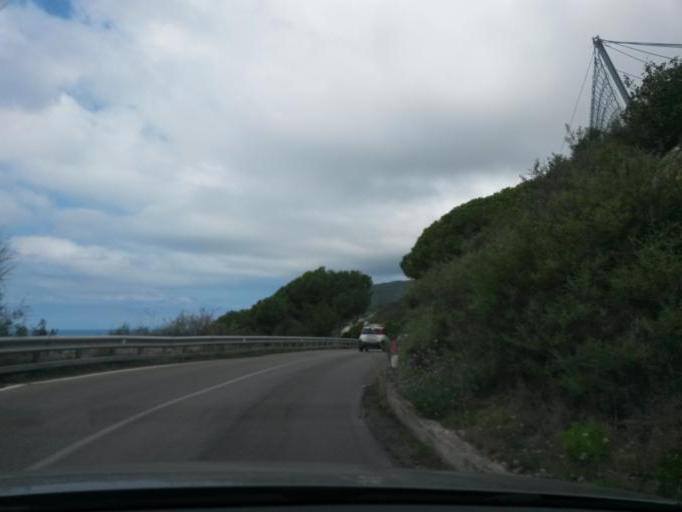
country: IT
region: Tuscany
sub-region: Provincia di Livorno
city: Marina di Campo
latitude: 42.7358
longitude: 10.1975
